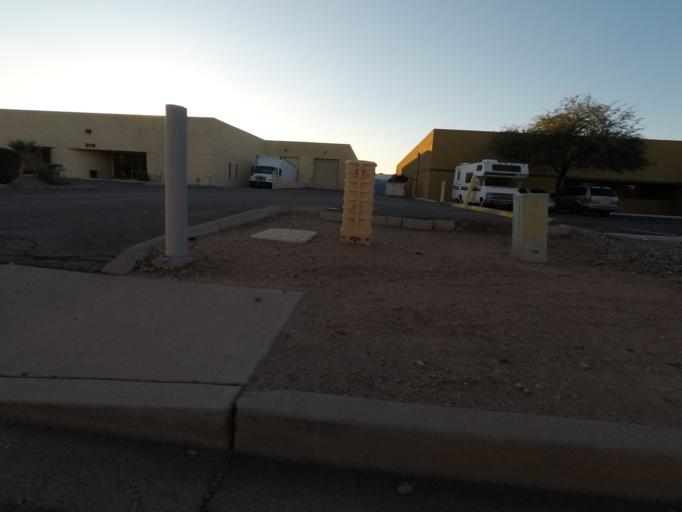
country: US
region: Arizona
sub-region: Maricopa County
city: Tempe Junction
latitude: 33.3945
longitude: -111.9479
